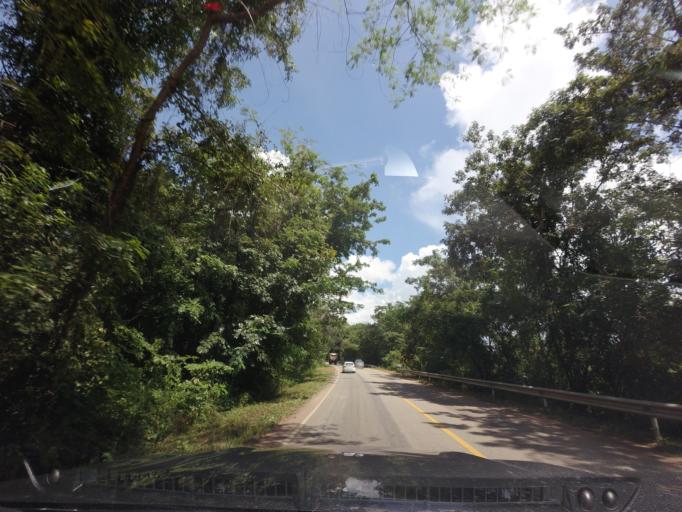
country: TH
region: Changwat Udon Thani
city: Phibun Rak
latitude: 17.5817
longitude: 103.0360
